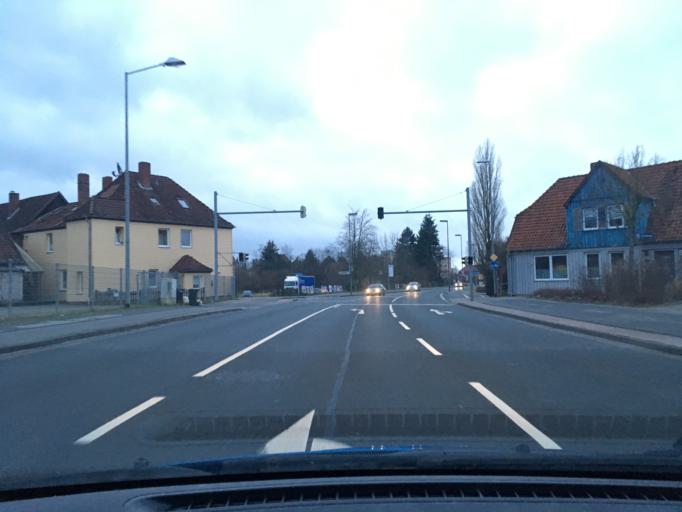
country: DE
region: Lower Saxony
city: Celle
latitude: 52.6325
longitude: 10.0866
